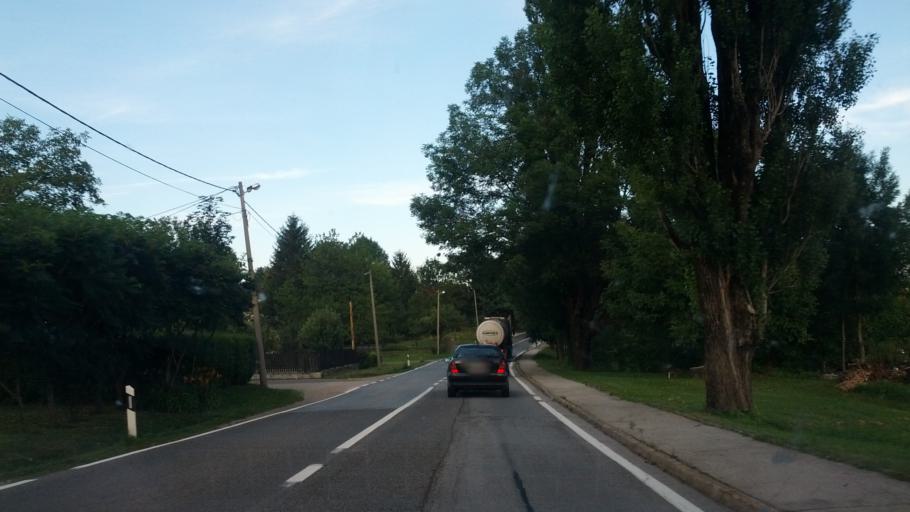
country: HR
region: Licko-Senjska
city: Jezerce
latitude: 44.9552
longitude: 15.6691
